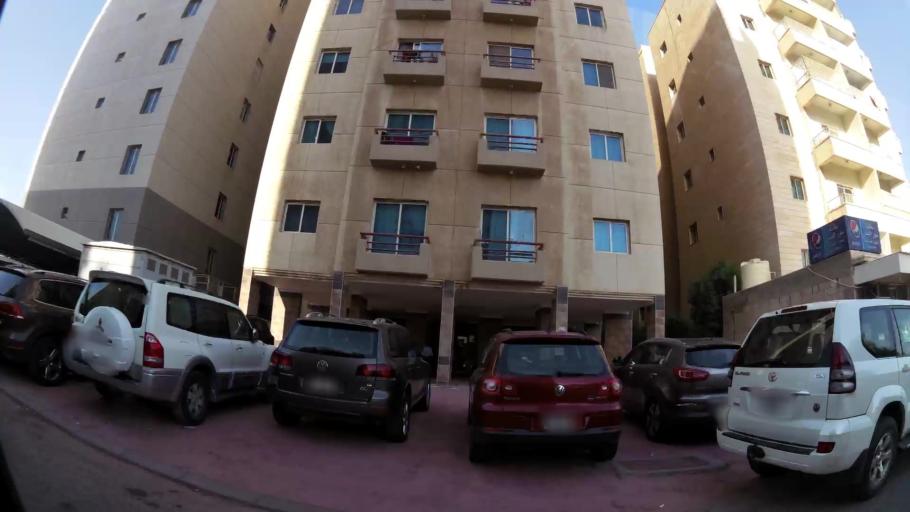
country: KW
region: Muhafazat Hawalli
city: As Salimiyah
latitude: 29.3364
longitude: 48.0816
